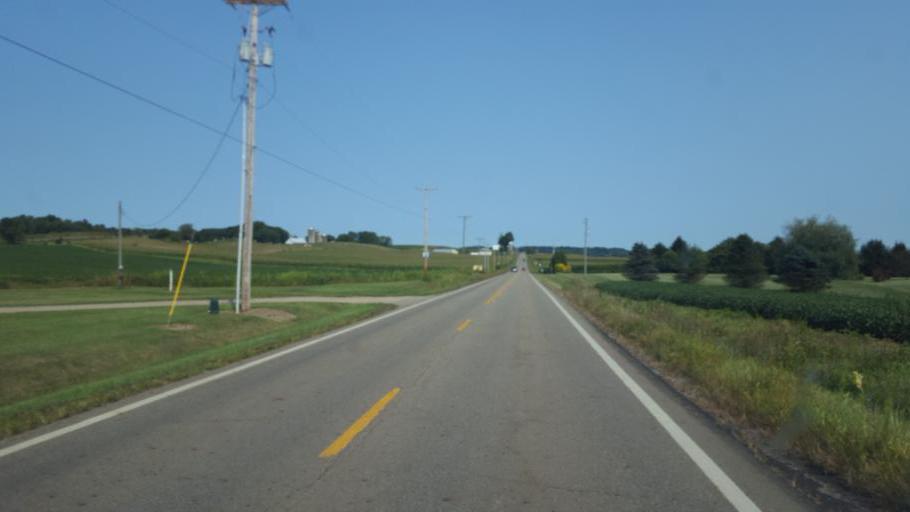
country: US
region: Ohio
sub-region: Ashland County
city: Loudonville
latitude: 40.6567
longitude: -82.1711
